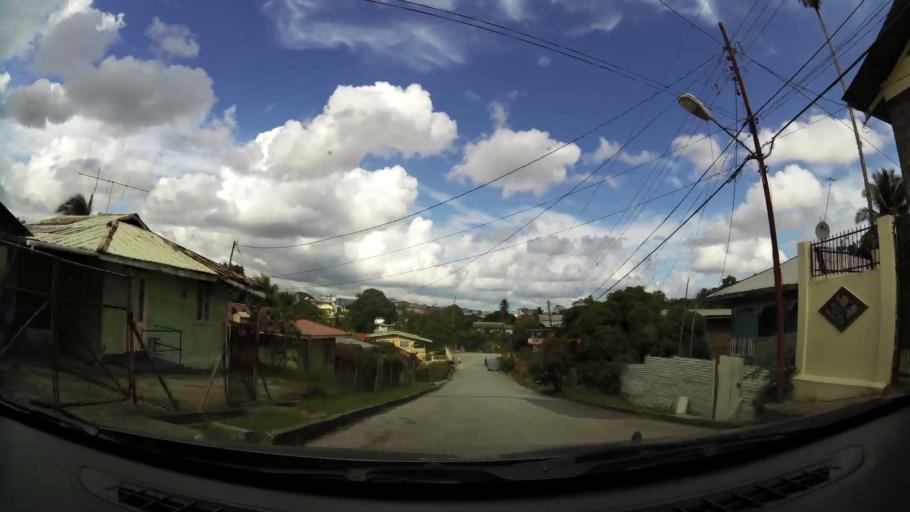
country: TT
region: City of San Fernando
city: Mon Repos
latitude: 10.2755
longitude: -61.4490
